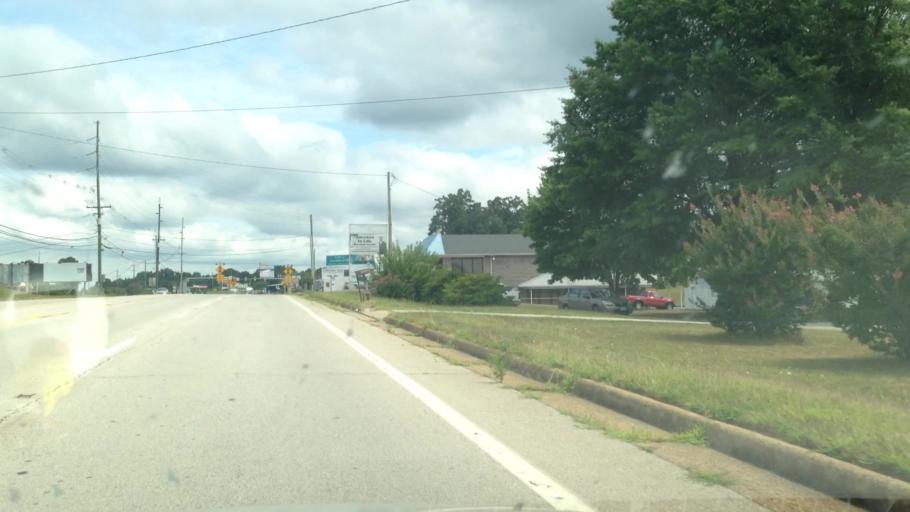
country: US
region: Virginia
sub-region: Pittsylvania County
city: Mount Hermon
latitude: 36.6864
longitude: -79.3691
